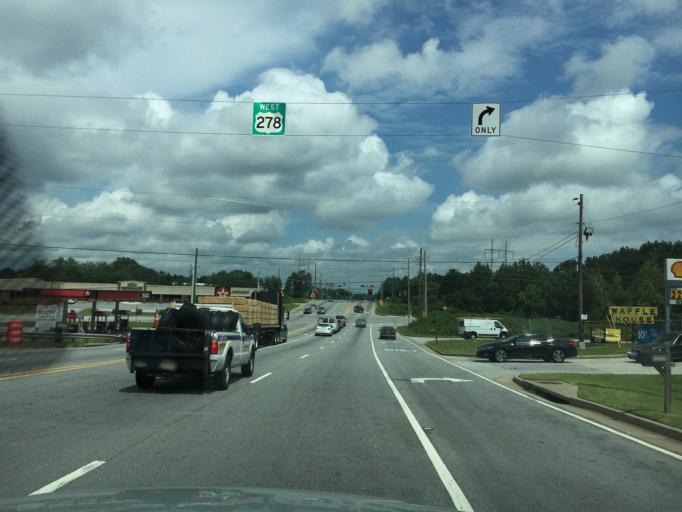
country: US
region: Georgia
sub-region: Rockdale County
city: Lakeview Estates
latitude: 33.6832
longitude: -84.0628
